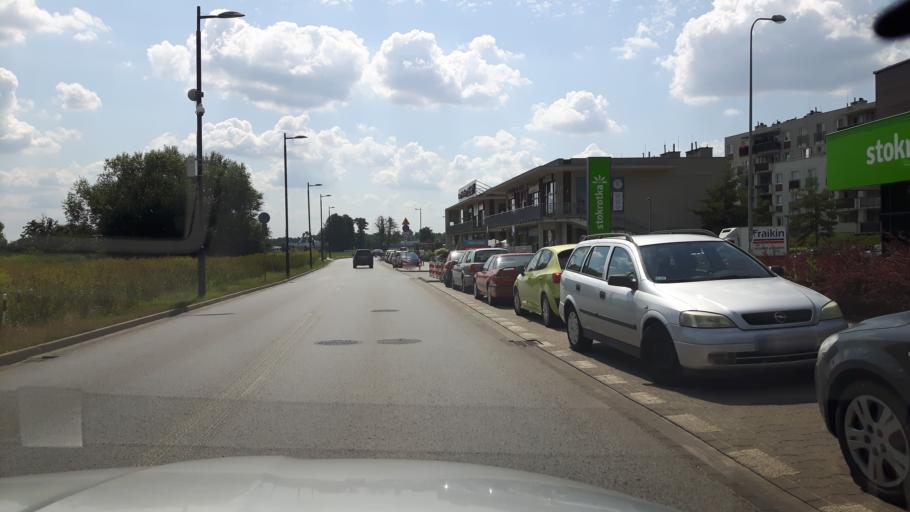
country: PL
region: Masovian Voivodeship
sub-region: Warszawa
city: Targowek
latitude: 52.3146
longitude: 21.0607
